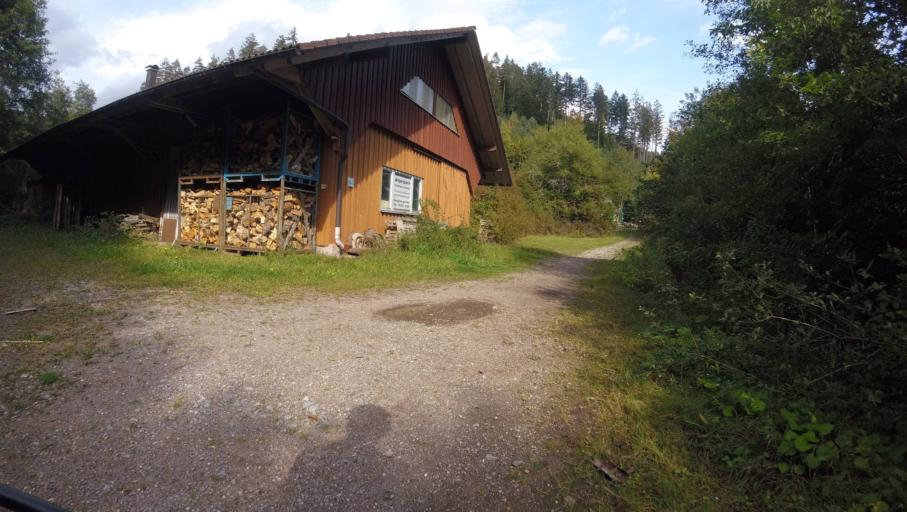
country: DE
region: Baden-Wuerttemberg
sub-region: Karlsruhe Region
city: Grombach
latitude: 48.5866
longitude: 8.5441
